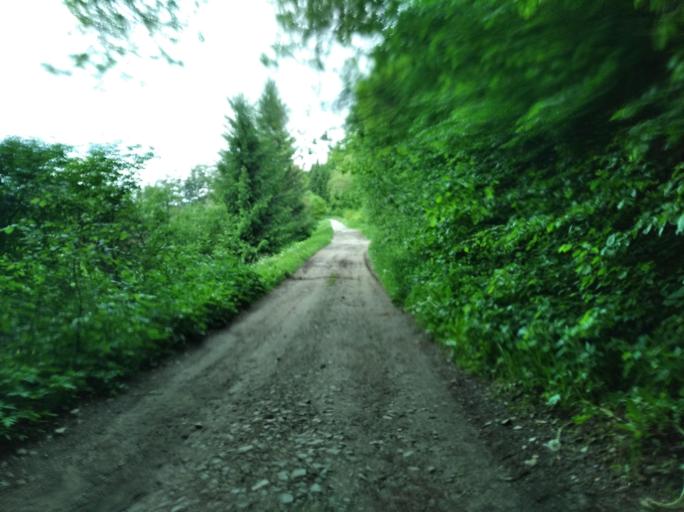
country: PL
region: Subcarpathian Voivodeship
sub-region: Powiat brzozowski
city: Jasionow
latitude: 49.6691
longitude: 21.9863
